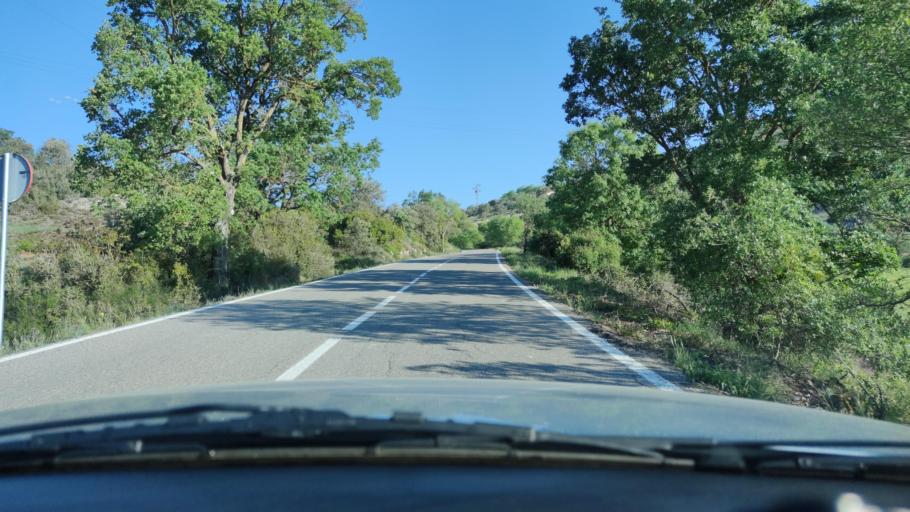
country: ES
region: Catalonia
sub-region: Provincia de Lleida
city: Artesa de Segre
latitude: 41.8788
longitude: 1.0138
